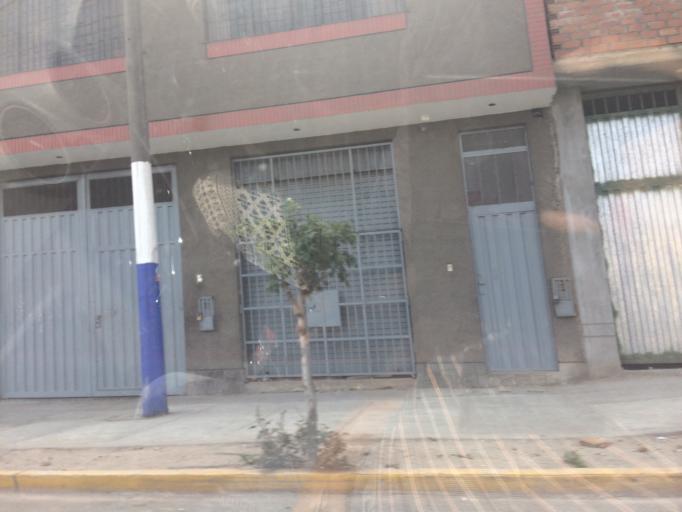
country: PE
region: Lima
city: Lima
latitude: -12.0308
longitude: -77.0420
